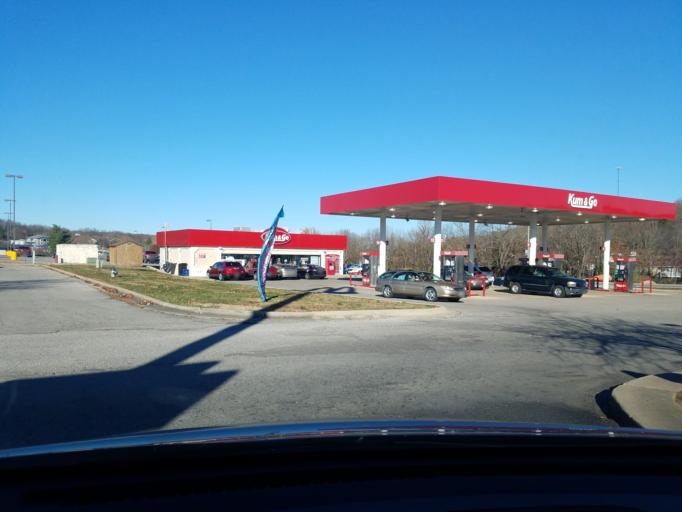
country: US
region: Missouri
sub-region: Pulaski County
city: Waynesville
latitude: 37.8088
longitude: -92.2244
